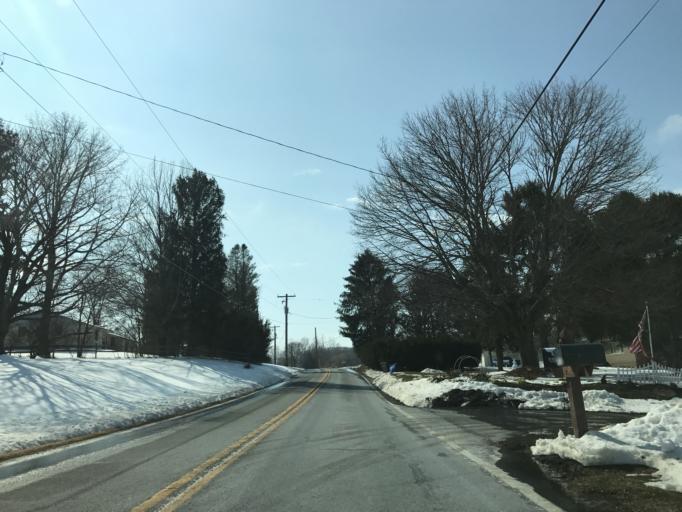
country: US
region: Pennsylvania
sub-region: York County
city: Susquehanna Trails
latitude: 39.7179
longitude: -76.3937
